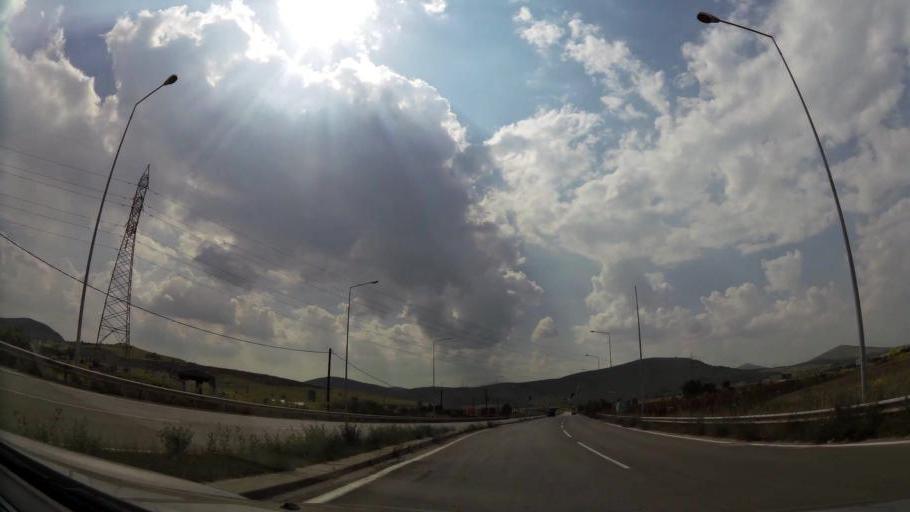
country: GR
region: West Macedonia
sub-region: Nomos Kozanis
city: Koila
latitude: 40.3420
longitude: 21.8120
